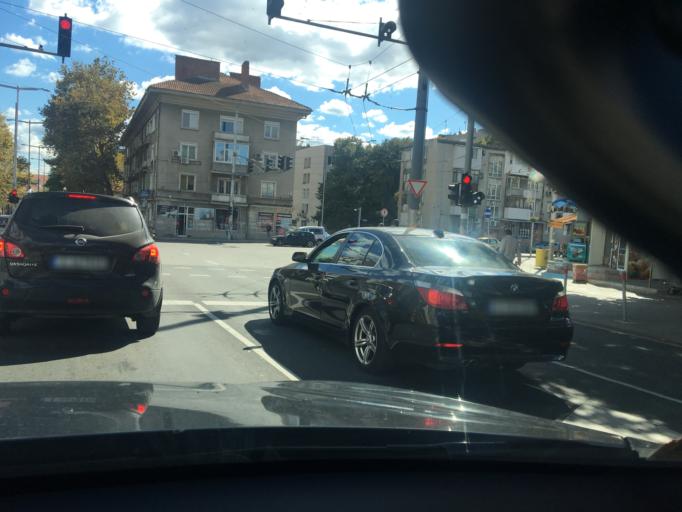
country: BG
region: Burgas
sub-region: Obshtina Burgas
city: Burgas
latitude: 42.5034
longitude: 27.4700
